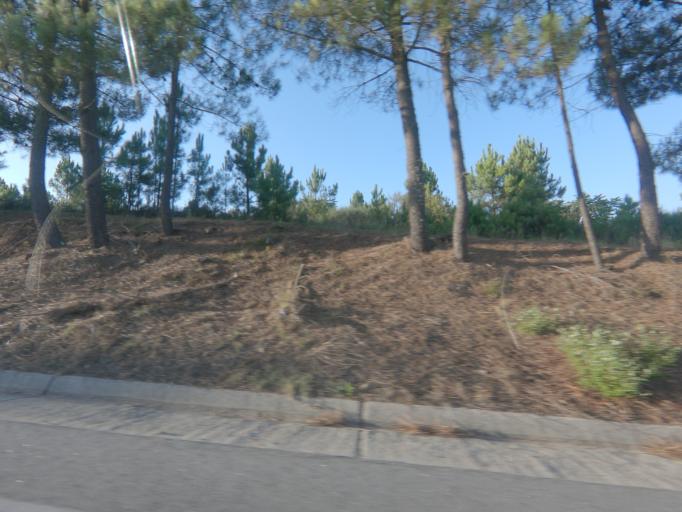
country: PT
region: Vila Real
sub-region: Sabrosa
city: Sabrosa
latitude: 41.2617
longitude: -7.6065
